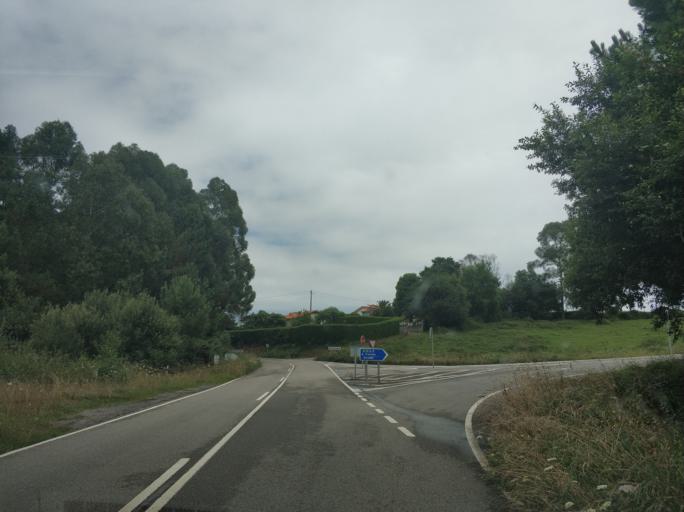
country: ES
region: Asturias
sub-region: Province of Asturias
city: Cudillero
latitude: 43.5581
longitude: -6.2859
